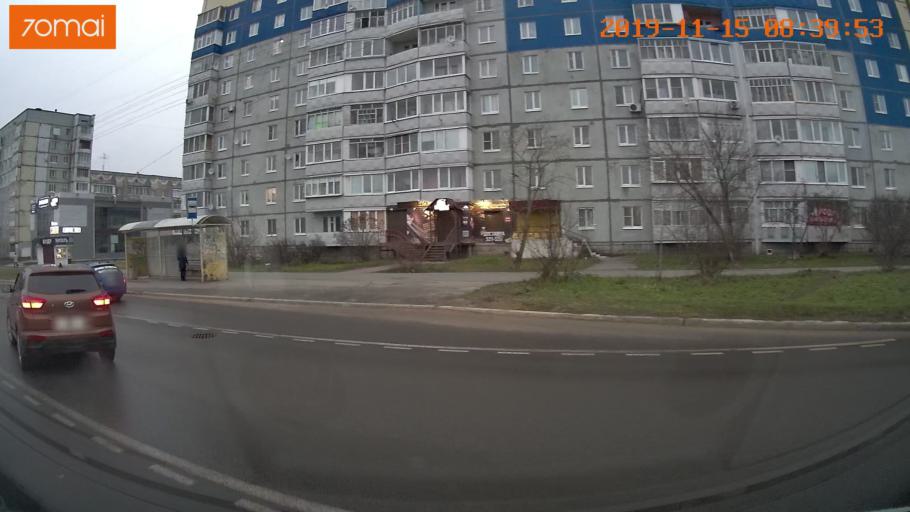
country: RU
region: Vologda
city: Cherepovets
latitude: 59.0936
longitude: 37.9194
